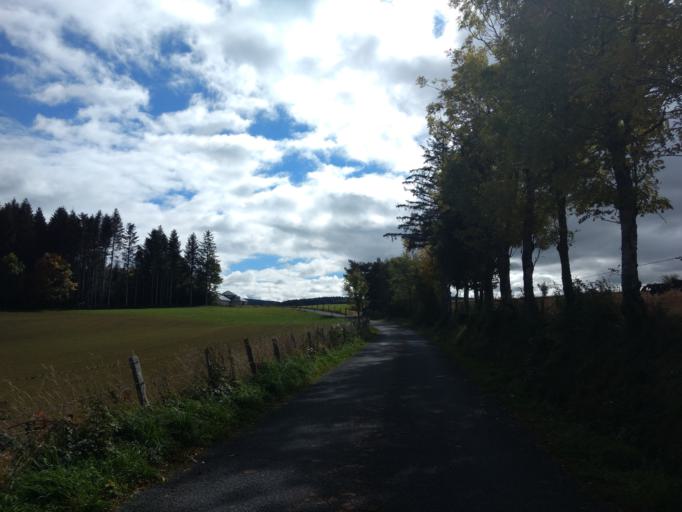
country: FR
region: Auvergne
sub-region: Departement du Cantal
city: Chaudes-Aigues
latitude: 44.8378
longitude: 2.9870
